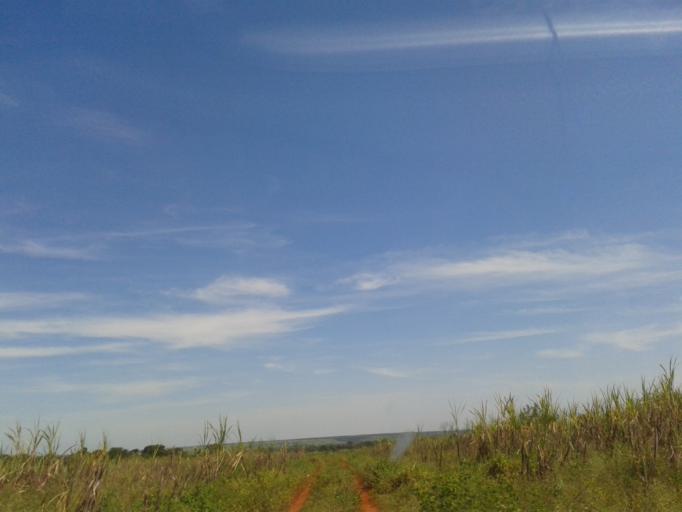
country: BR
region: Minas Gerais
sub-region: Santa Vitoria
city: Santa Vitoria
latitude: -19.1609
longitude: -50.5445
